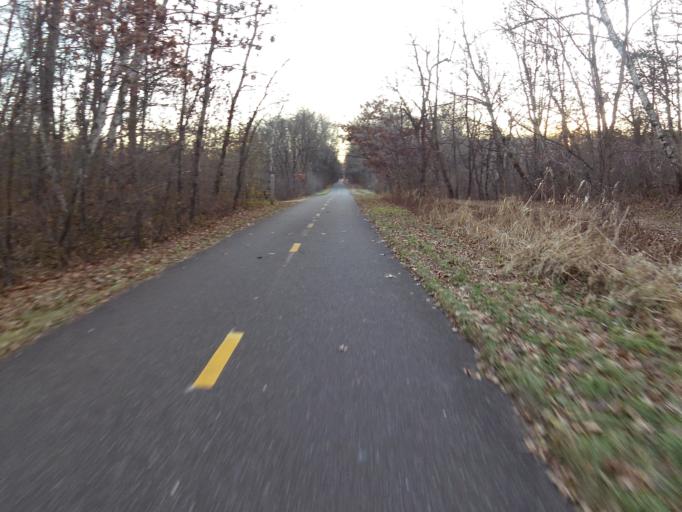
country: US
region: Minnesota
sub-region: Washington County
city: Grant
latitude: 45.0839
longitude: -92.8936
